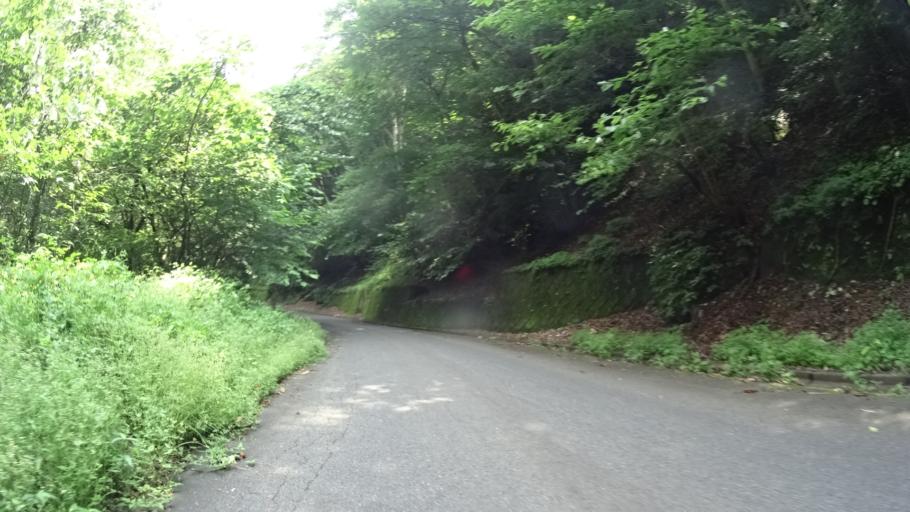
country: JP
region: Gunma
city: Tomioka
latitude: 36.0841
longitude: 138.7080
